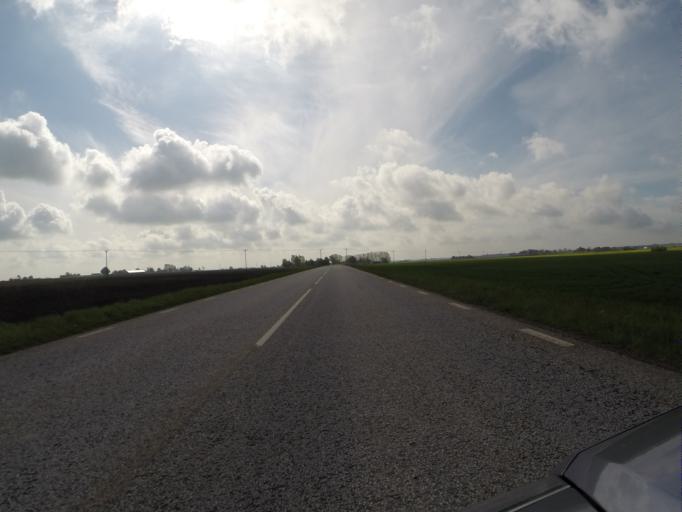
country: SE
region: Skane
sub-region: Landskrona
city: Asmundtorp
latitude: 55.8771
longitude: 12.9780
